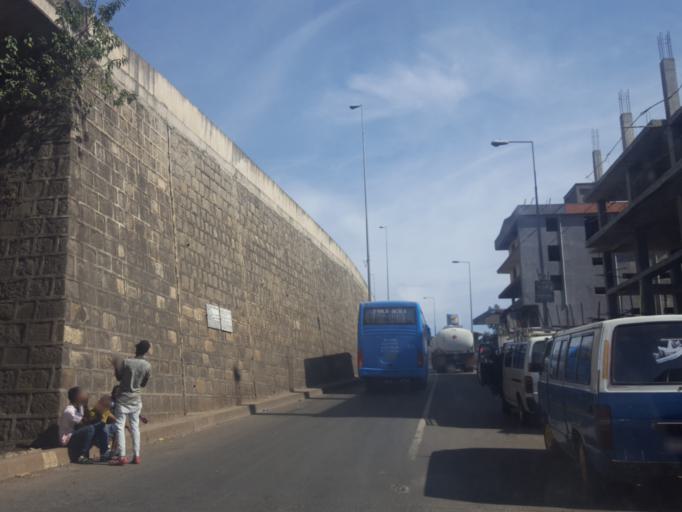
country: ET
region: Adis Abeba
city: Addis Ababa
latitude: 9.0570
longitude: 38.7136
